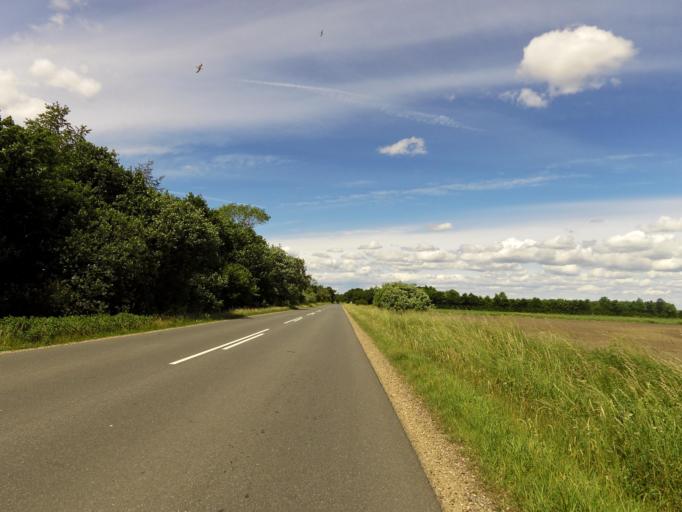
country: DK
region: South Denmark
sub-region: Esbjerg Kommune
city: Ribe
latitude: 55.2827
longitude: 8.7878
